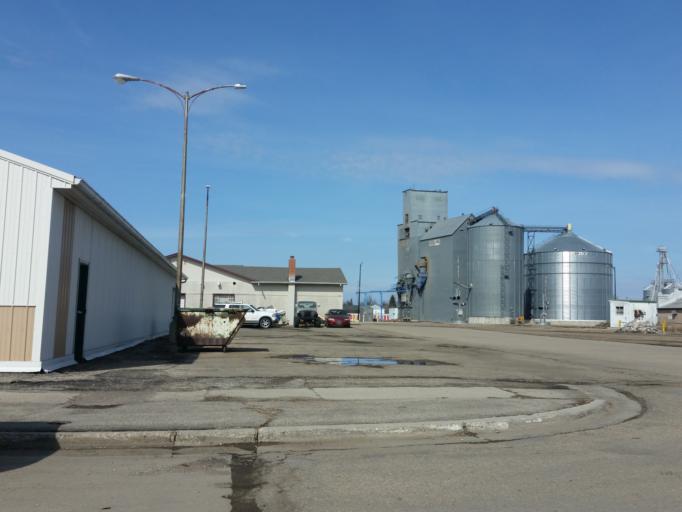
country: US
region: North Dakota
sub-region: Walsh County
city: Grafton
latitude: 48.4176
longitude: -97.4099
